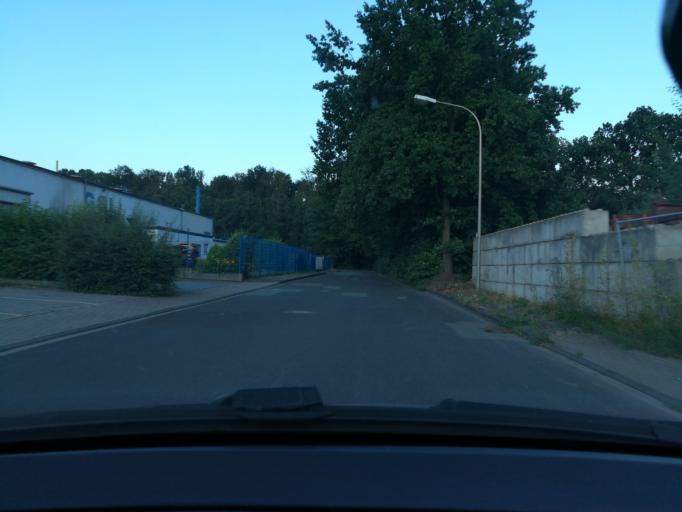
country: DE
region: North Rhine-Westphalia
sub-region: Regierungsbezirk Munster
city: Lienen
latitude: 52.1488
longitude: 7.9858
